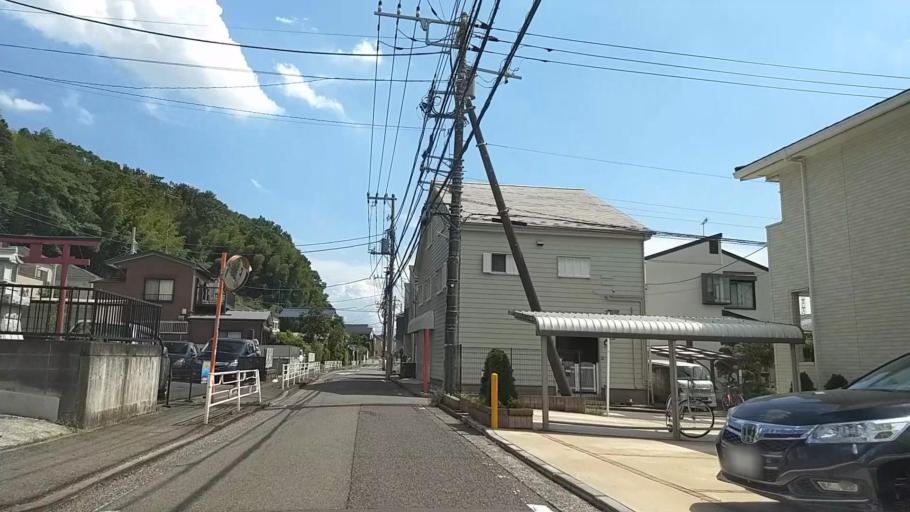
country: JP
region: Kanagawa
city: Yokohama
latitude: 35.5206
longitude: 139.5791
